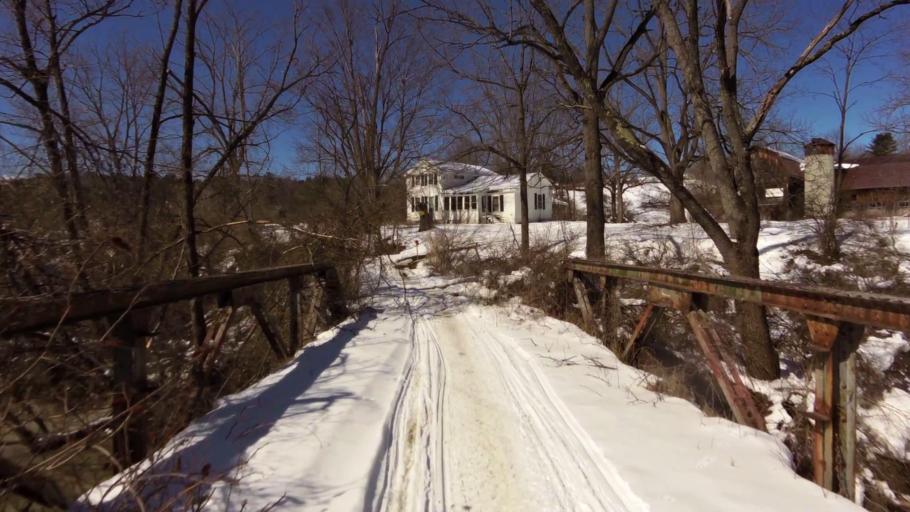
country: US
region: New York
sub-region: Allegany County
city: Houghton
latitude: 42.3604
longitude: -78.1489
